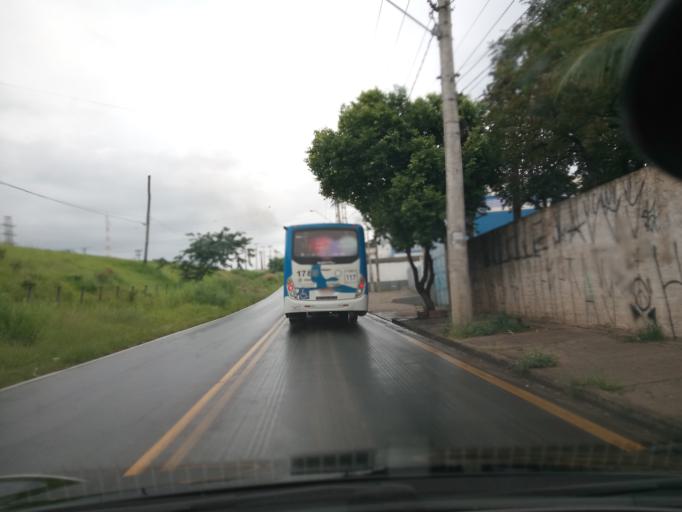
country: BR
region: Sao Paulo
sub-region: Campinas
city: Campinas
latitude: -22.9762
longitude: -47.1038
